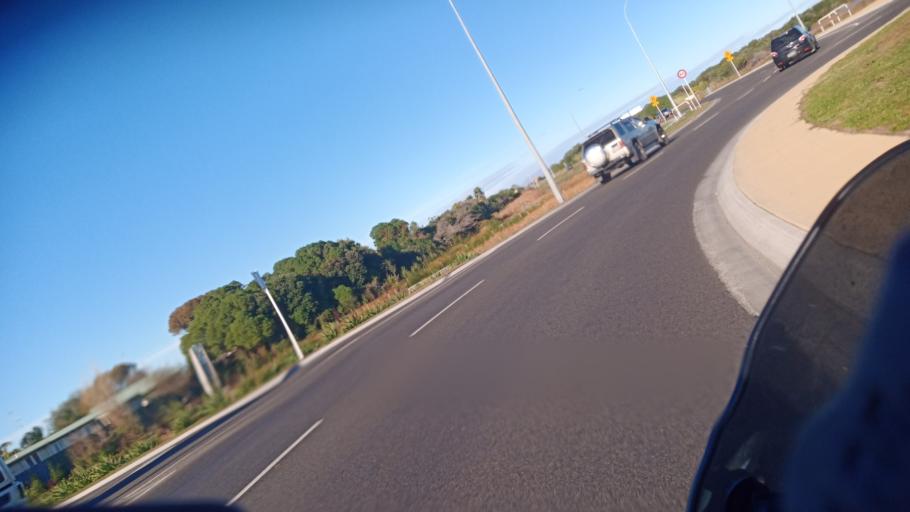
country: NZ
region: Hawke's Bay
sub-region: Napier City
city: Napier
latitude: -39.4748
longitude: 176.8774
